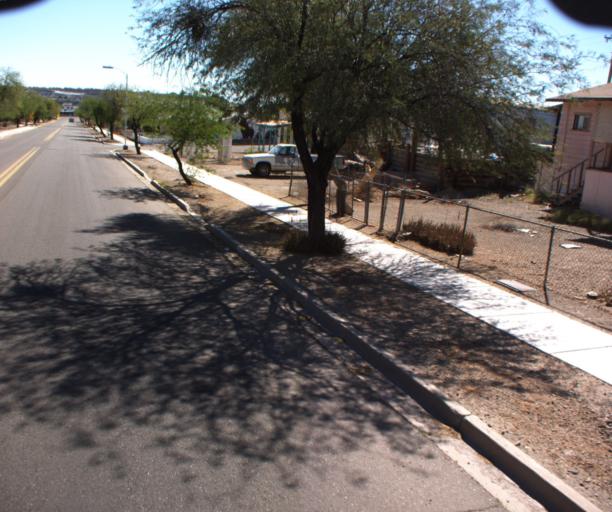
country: US
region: Arizona
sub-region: Pima County
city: Ajo
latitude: 32.3748
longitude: -112.8678
